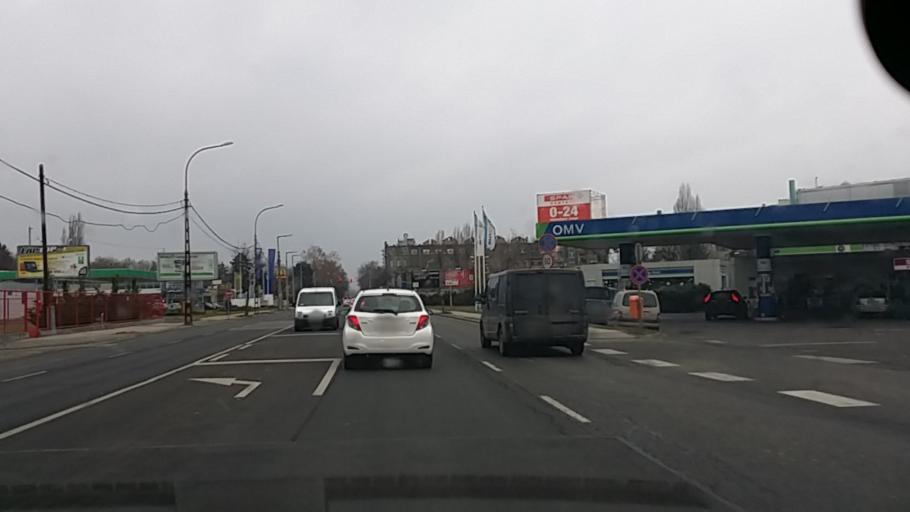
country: HU
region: Budapest
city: Budapest IV. keruelet
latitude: 47.5740
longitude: 19.0811
